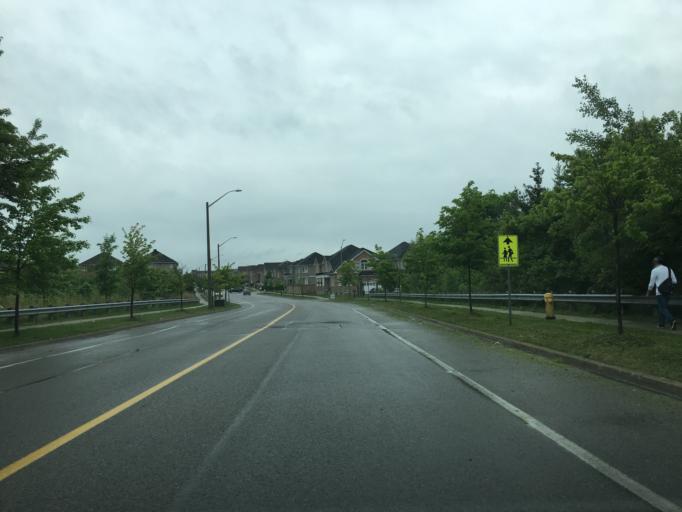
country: CA
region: Ontario
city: Markham
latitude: 43.8406
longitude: -79.2467
